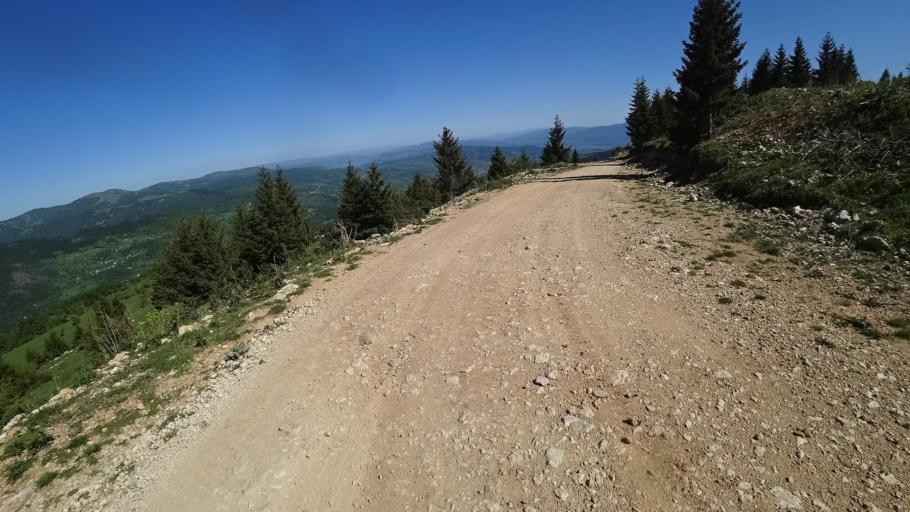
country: BA
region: Federation of Bosnia and Herzegovina
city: Travnik
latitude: 44.2878
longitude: 17.6943
